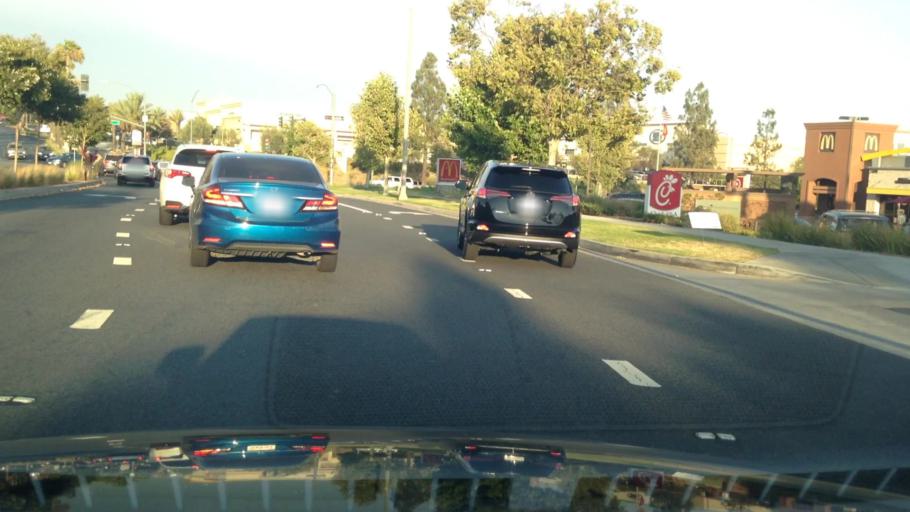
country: US
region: California
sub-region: Riverside County
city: Moreno Valley
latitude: 33.9397
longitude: -117.2801
